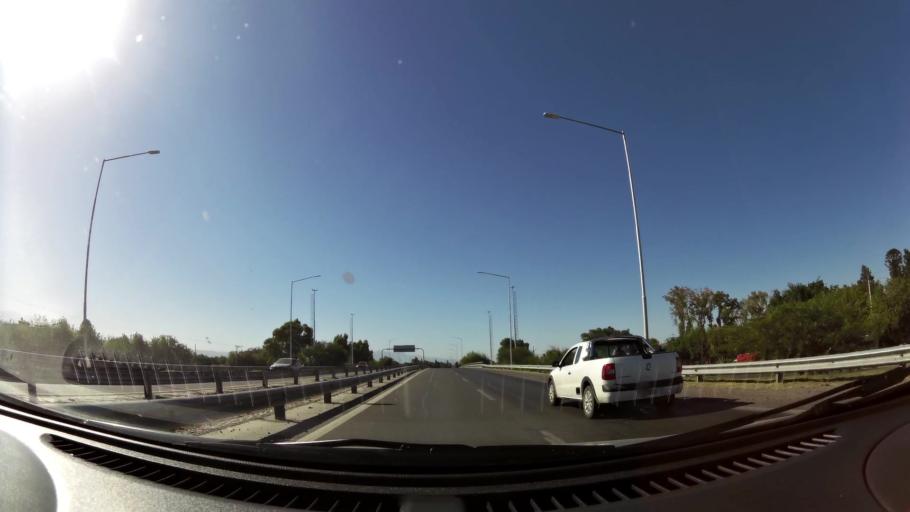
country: AR
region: San Juan
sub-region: Departamento de Santa Lucia
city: Santa Lucia
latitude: -31.5342
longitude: -68.5041
